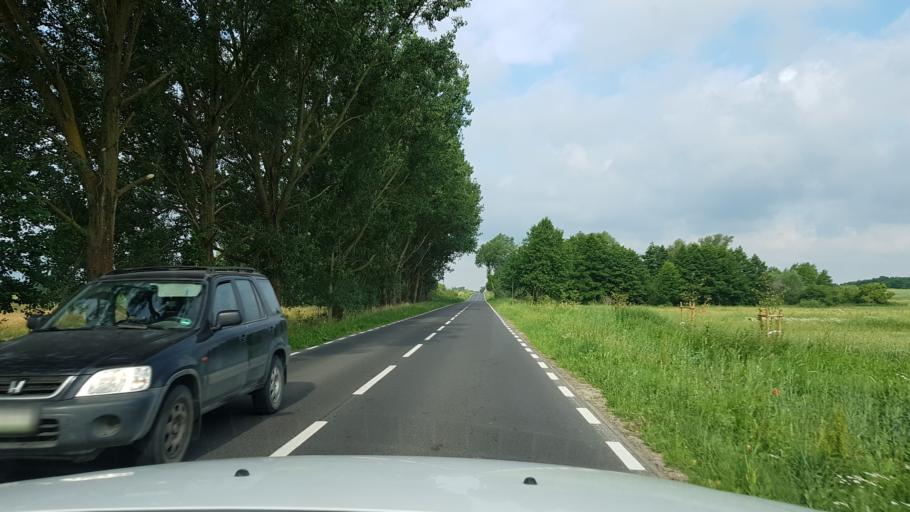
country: PL
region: West Pomeranian Voivodeship
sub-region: Powiat gryfinski
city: Gryfino
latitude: 53.2616
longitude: 14.6033
